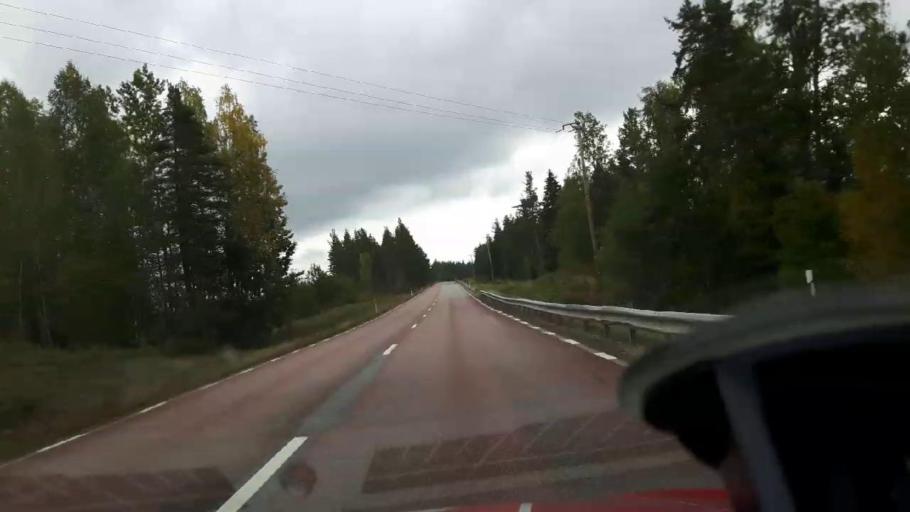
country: SE
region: Gaevleborg
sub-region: Soderhamns Kommun
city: Soderhamn
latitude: 61.1276
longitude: 16.9290
